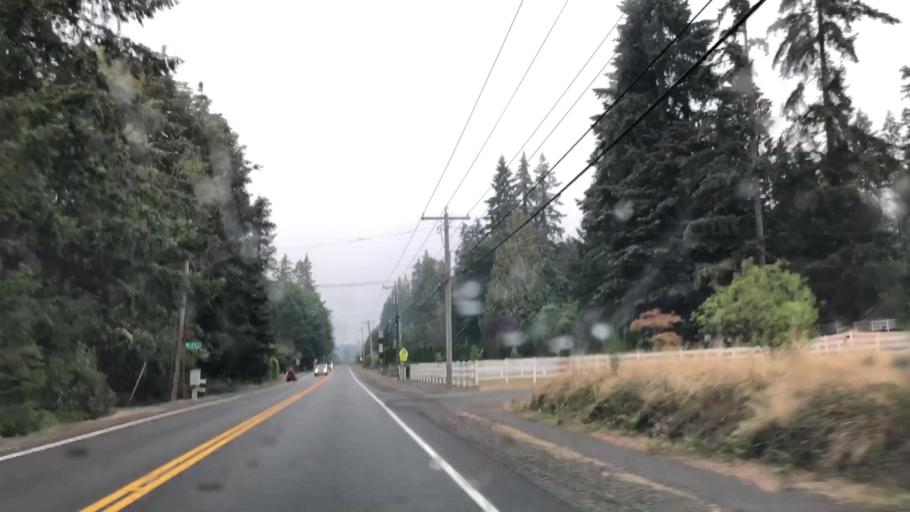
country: US
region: Washington
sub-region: King County
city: Cottage Lake
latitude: 47.7388
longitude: -122.0489
